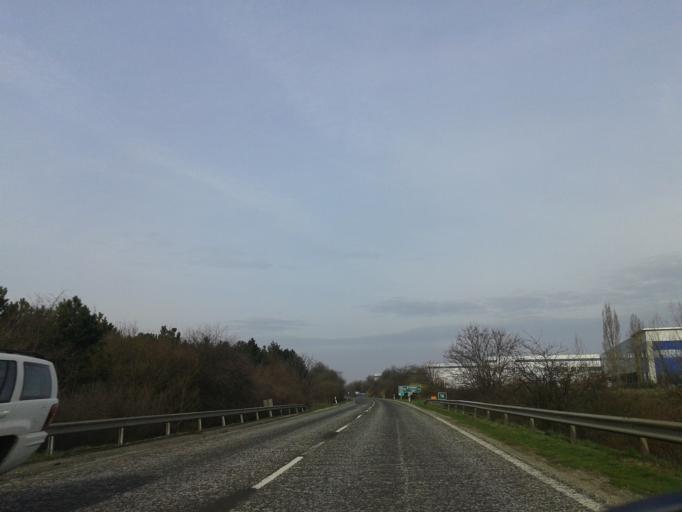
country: HU
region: Pest
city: Biatorbagy
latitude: 47.4900
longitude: 18.8238
